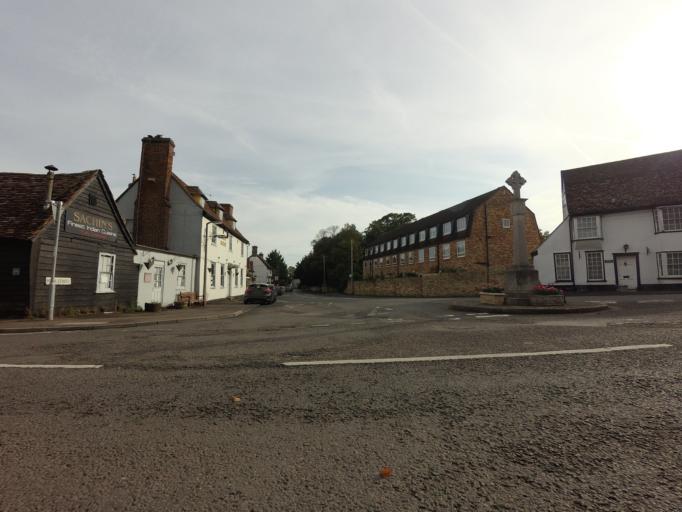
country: GB
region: England
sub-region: Cambridgeshire
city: Harston
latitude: 52.0926
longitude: 0.0722
